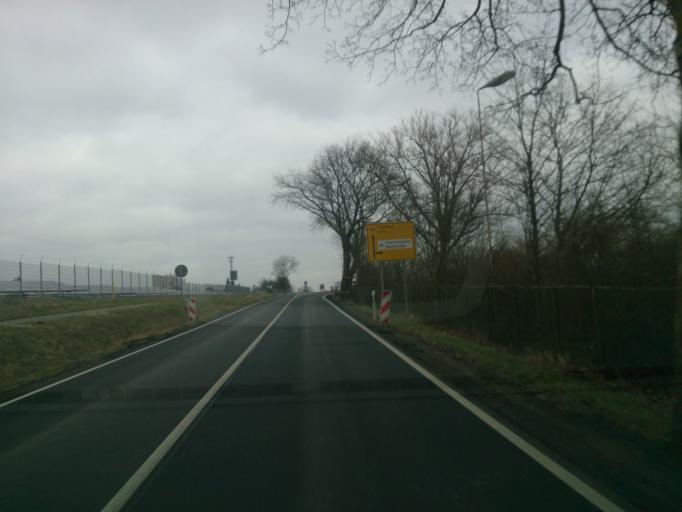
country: DE
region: Mecklenburg-Vorpommern
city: Demmin
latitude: 53.9191
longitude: 13.0334
